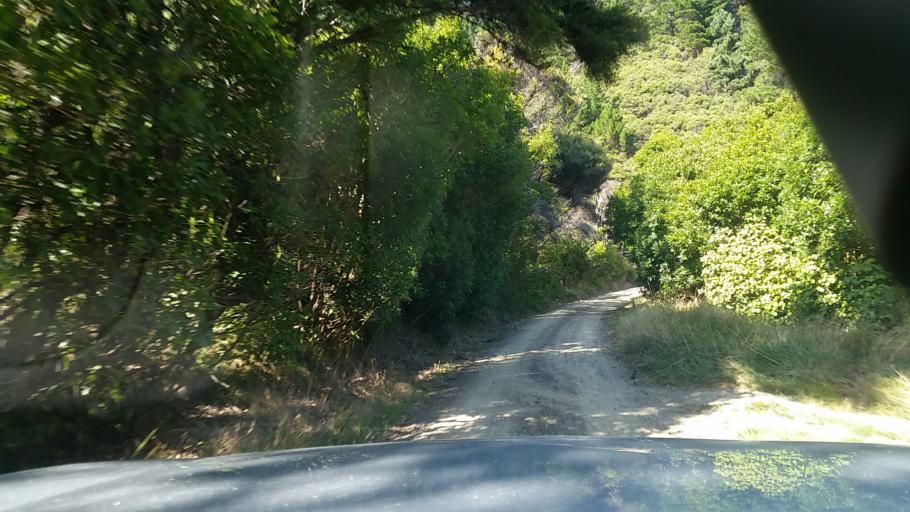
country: NZ
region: Marlborough
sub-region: Marlborough District
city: Picton
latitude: -41.3041
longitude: 174.1777
